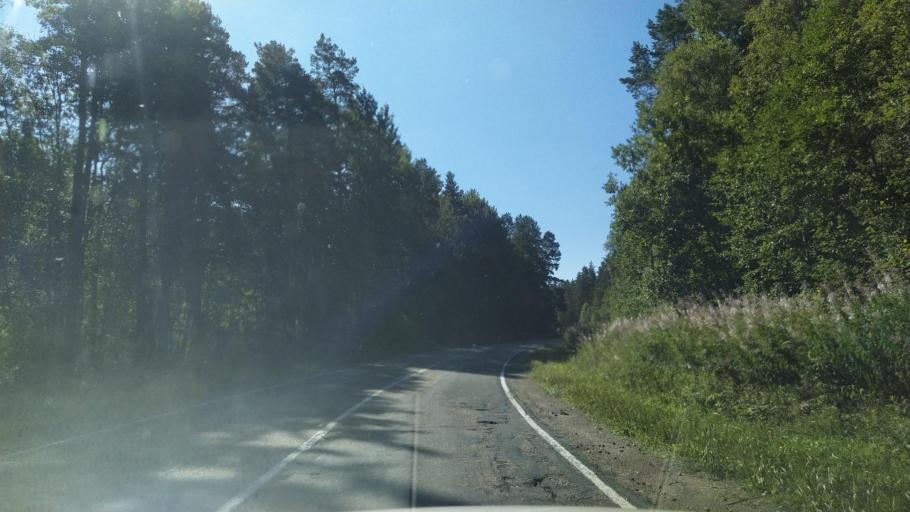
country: RU
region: Leningrad
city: Priozersk
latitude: 60.9739
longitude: 30.2815
